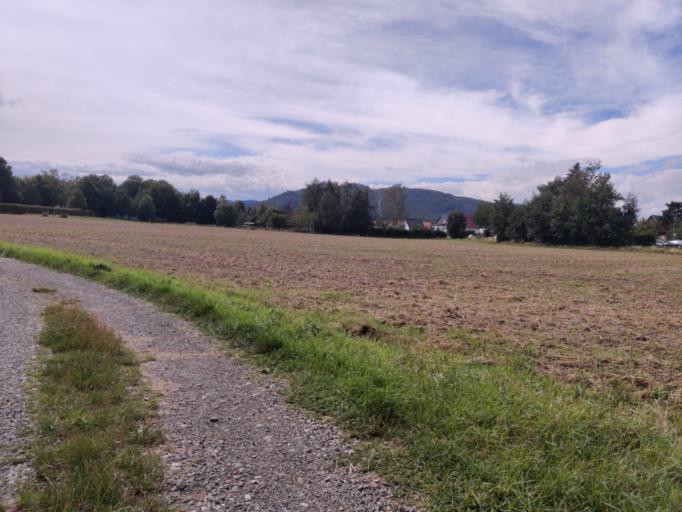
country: DE
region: Lower Saxony
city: Langelsheim
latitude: 51.9407
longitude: 10.3439
